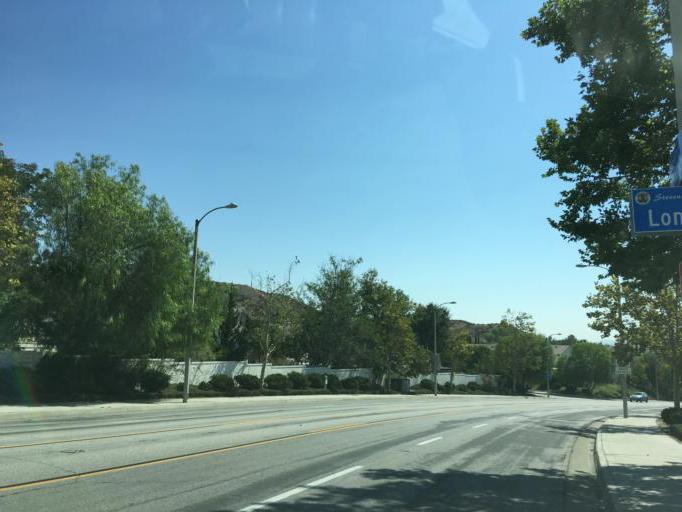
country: US
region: California
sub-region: Los Angeles County
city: Santa Clarita
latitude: 34.3911
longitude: -118.5867
